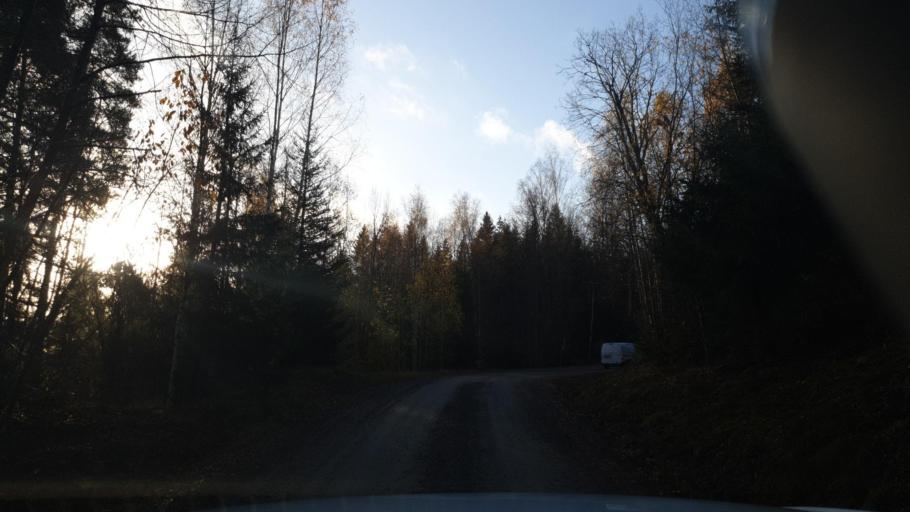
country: SE
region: Vaermland
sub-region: Grums Kommun
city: Grums
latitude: 59.4760
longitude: 12.9288
